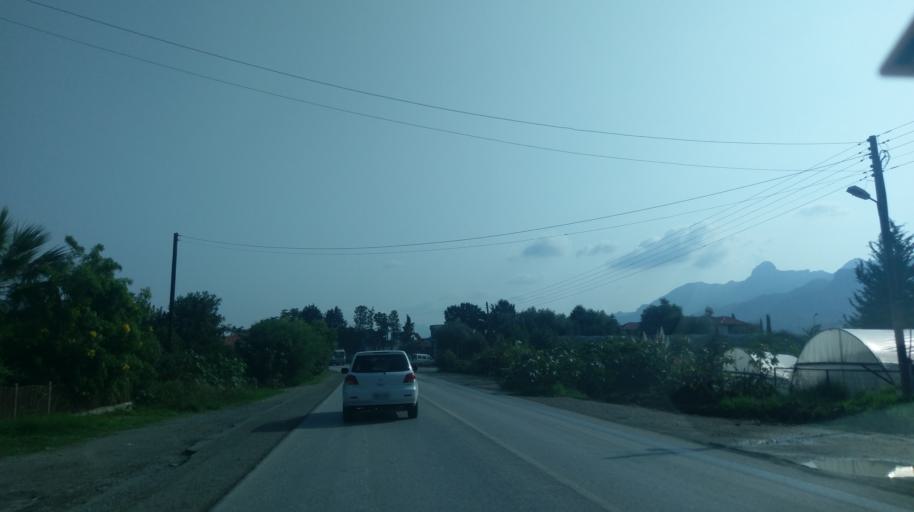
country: CY
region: Keryneia
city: Kyrenia
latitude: 35.3296
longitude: 33.3519
